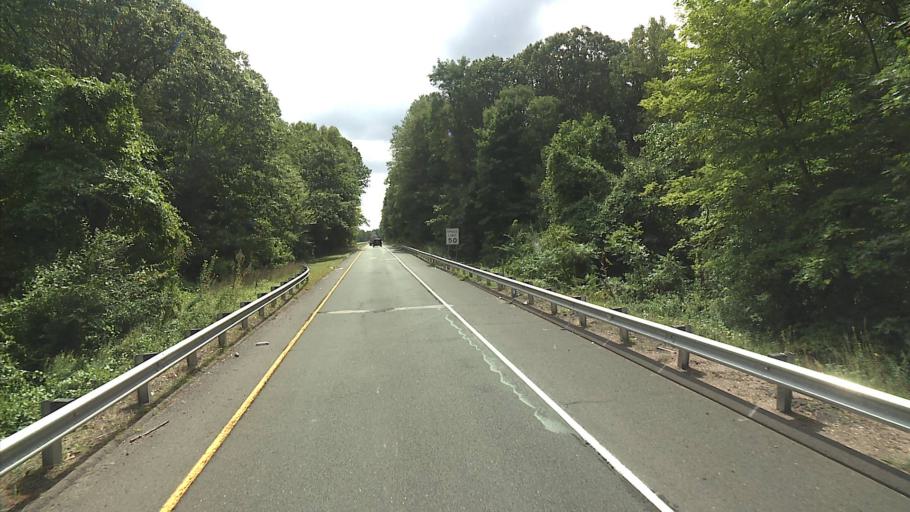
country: US
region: Connecticut
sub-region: Hartford County
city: Tariffville
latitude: 41.8955
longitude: -72.7522
